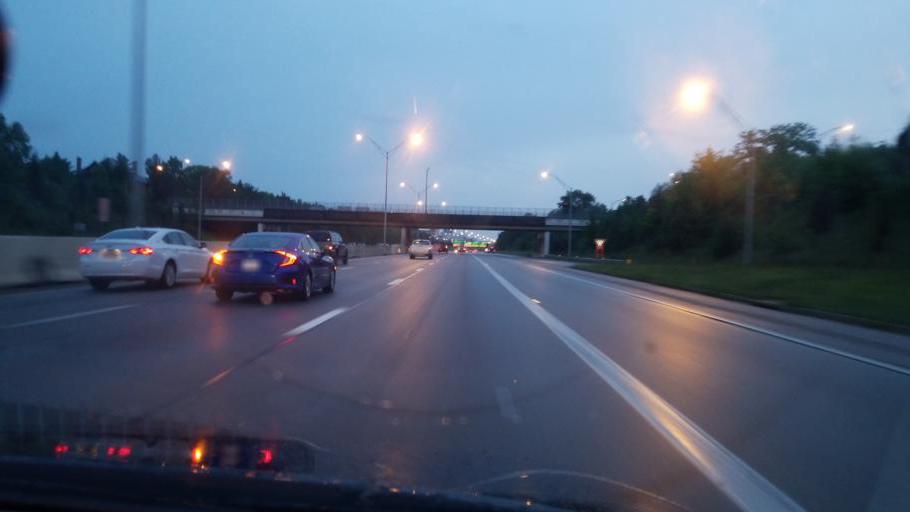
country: US
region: Ohio
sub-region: Franklin County
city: Bexley
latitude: 39.9537
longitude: -82.9639
